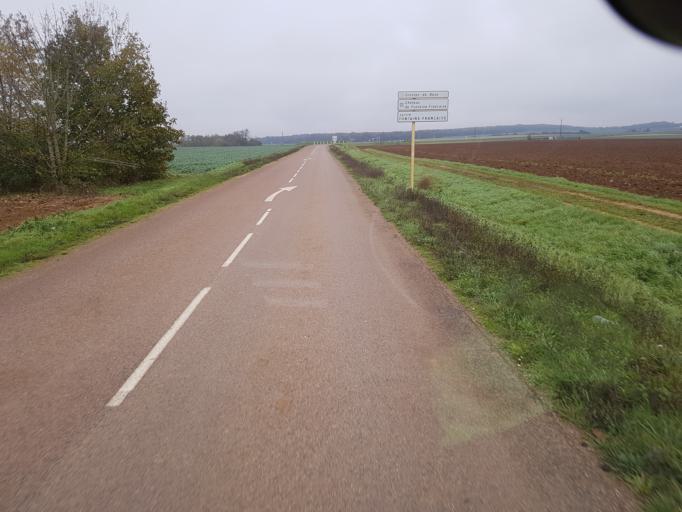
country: FR
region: Bourgogne
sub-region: Departement de la Cote-d'Or
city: Saint-Julien
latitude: 47.4272
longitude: 5.2095
